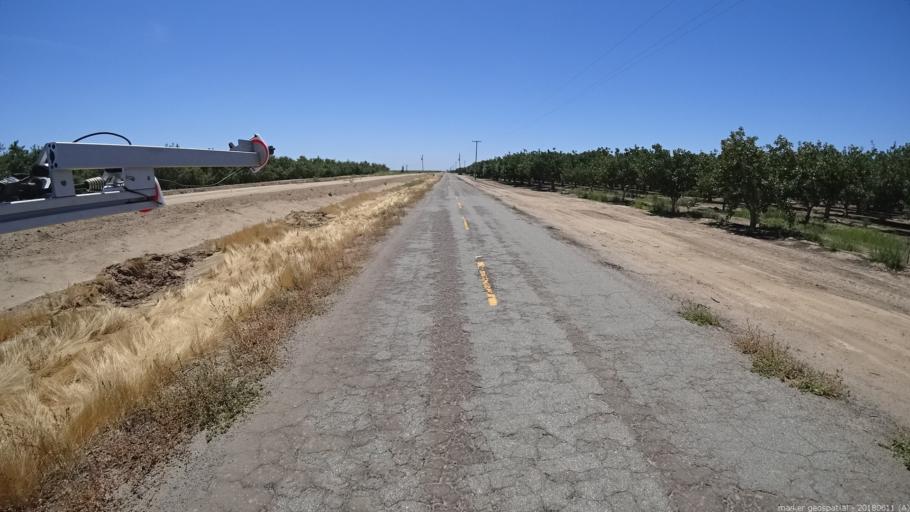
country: US
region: California
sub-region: Madera County
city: Fairmead
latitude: 37.0495
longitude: -120.2205
